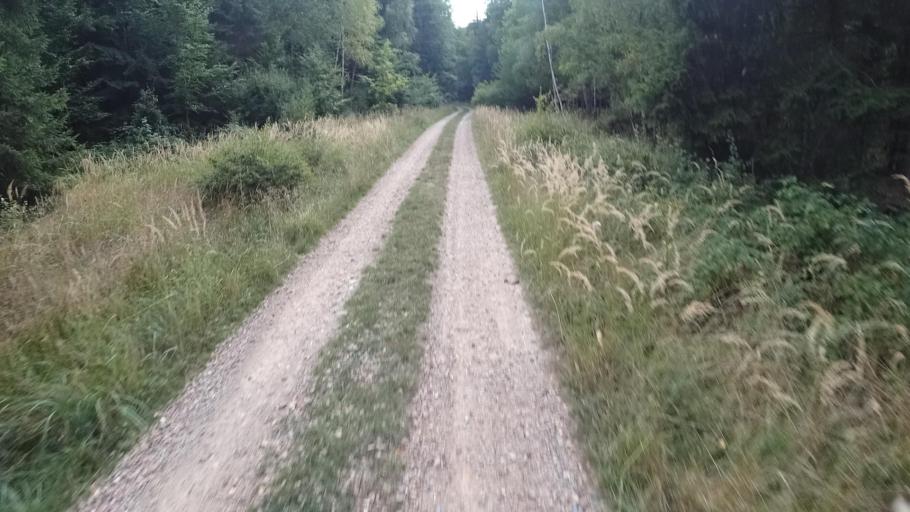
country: DE
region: Rheinland-Pfalz
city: Dichtelbach
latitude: 50.0127
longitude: 7.7121
